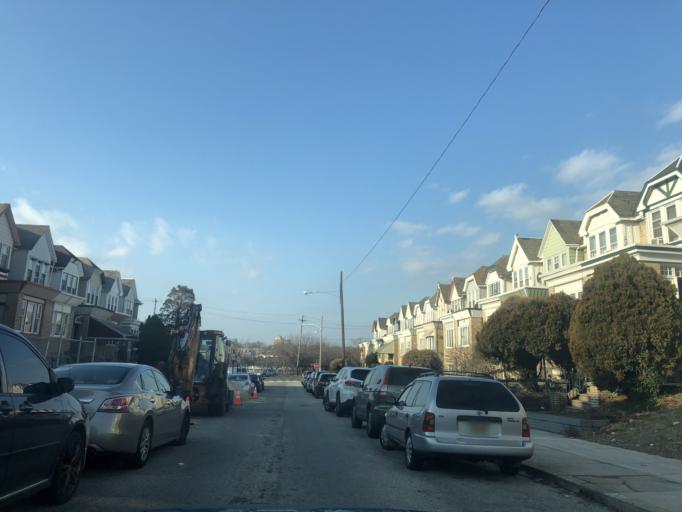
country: US
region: Pennsylvania
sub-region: Montgomery County
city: Bala-Cynwyd
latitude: 39.9838
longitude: -75.2326
